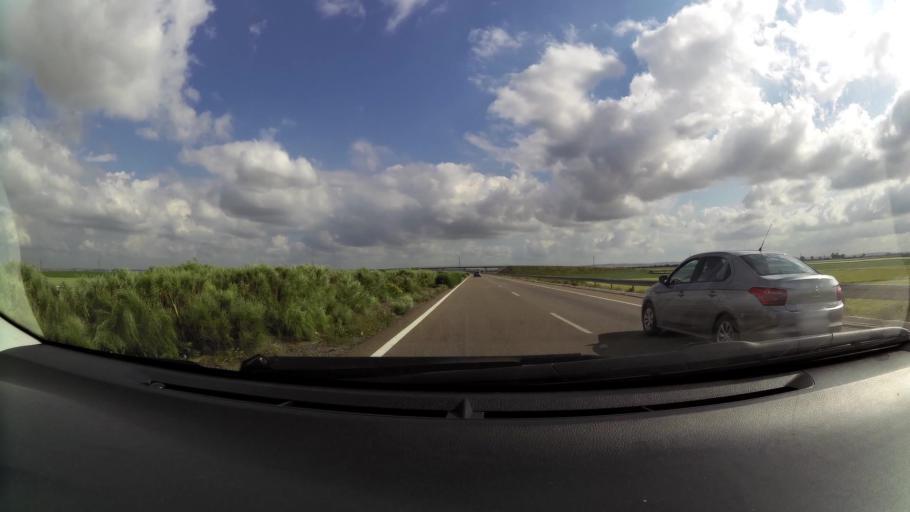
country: MA
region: Chaouia-Ouardigha
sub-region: Settat Province
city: Berrechid
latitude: 33.1812
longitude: -7.5732
